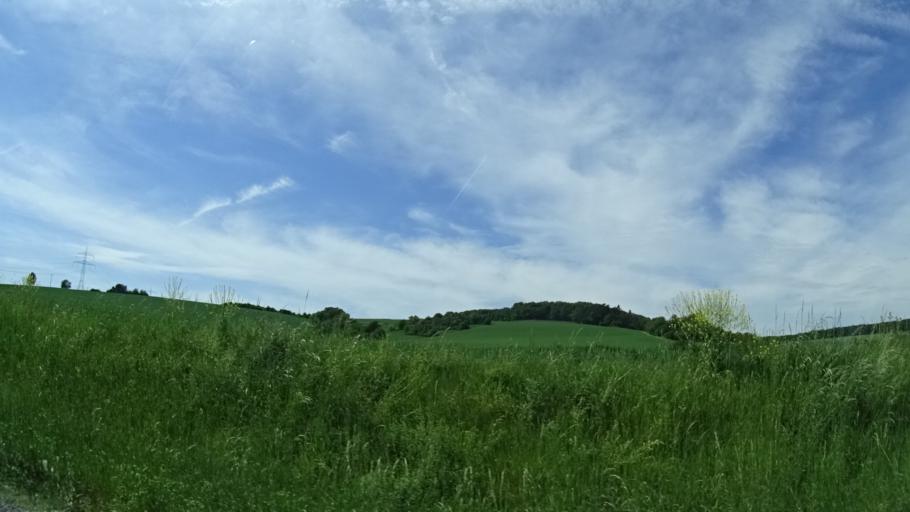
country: DE
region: Bavaria
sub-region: Regierungsbezirk Unterfranken
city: Arnstein
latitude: 49.9888
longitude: 9.9802
